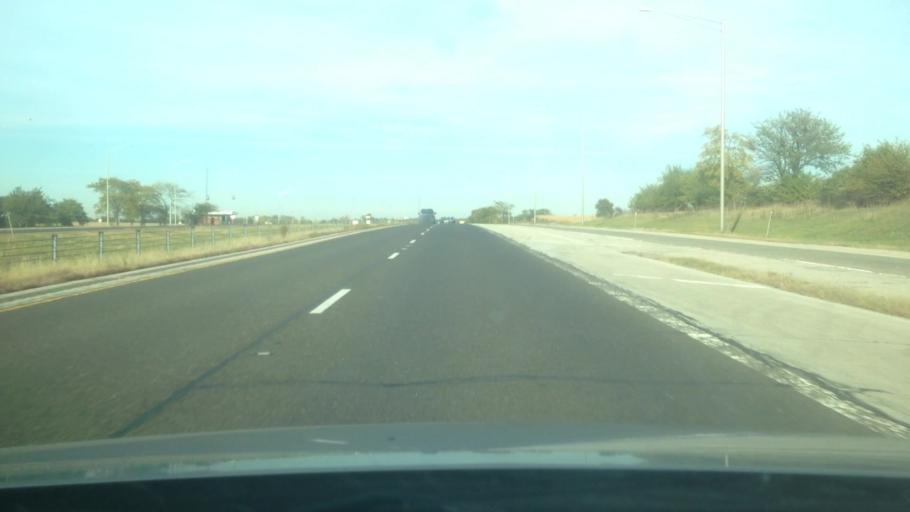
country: US
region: Illinois
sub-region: Will County
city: Peotone
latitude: 41.3636
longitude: -87.8014
